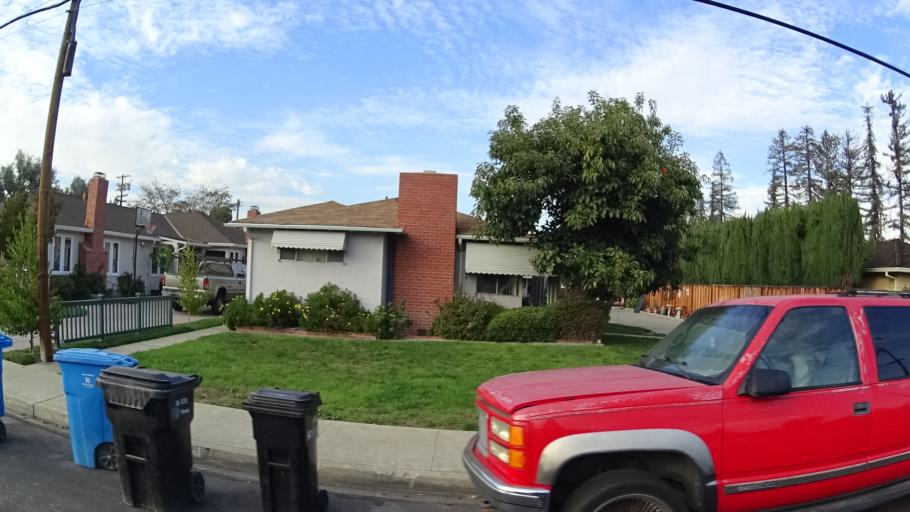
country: US
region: California
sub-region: Santa Clara County
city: Santa Clara
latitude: 37.3437
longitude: -121.9583
